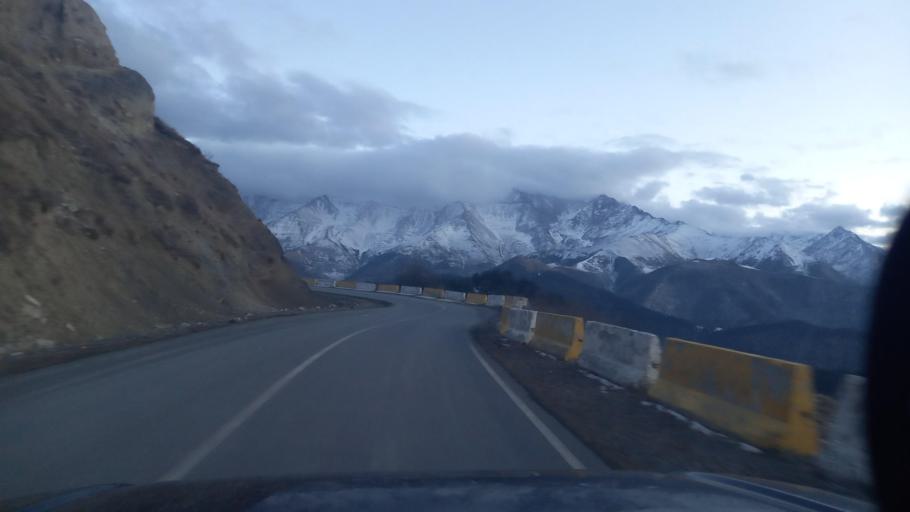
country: RU
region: Ingushetiya
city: Dzhayrakh
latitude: 42.8199
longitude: 44.8350
